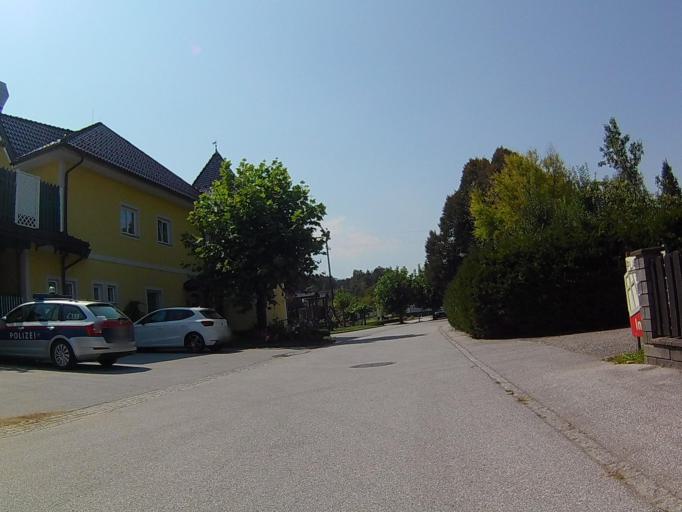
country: AT
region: Styria
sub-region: Politischer Bezirk Deutschlandsberg
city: Pitschgau
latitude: 46.6946
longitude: 15.2629
